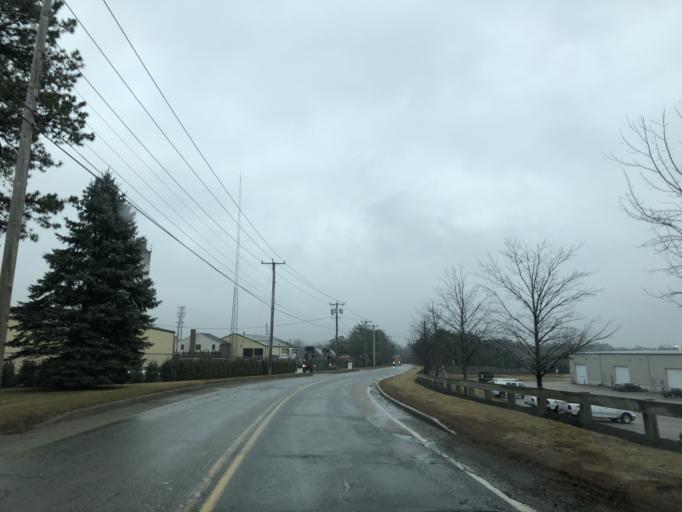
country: US
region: Massachusetts
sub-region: Norfolk County
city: Plainville
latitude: 42.0074
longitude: -71.2938
